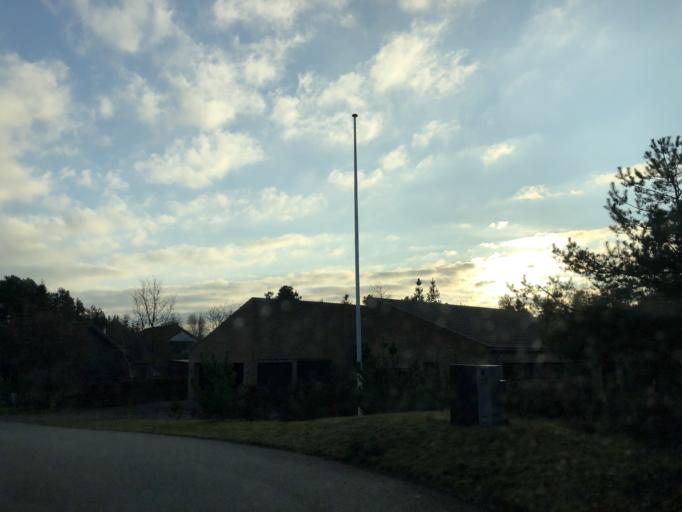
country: DK
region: Central Jutland
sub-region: Holstebro Kommune
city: Ulfborg
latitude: 56.3201
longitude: 8.4352
